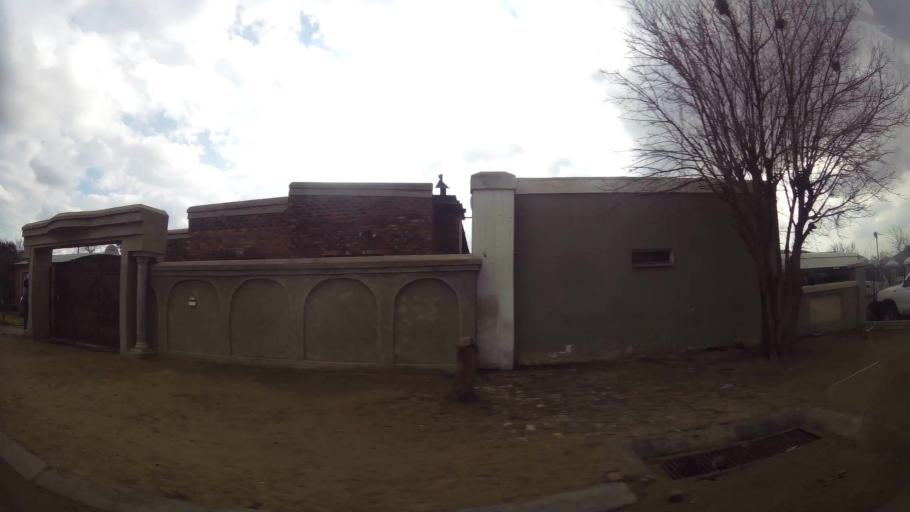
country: ZA
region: Orange Free State
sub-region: Fezile Dabi District Municipality
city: Sasolburg
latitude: -26.8450
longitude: 27.8644
